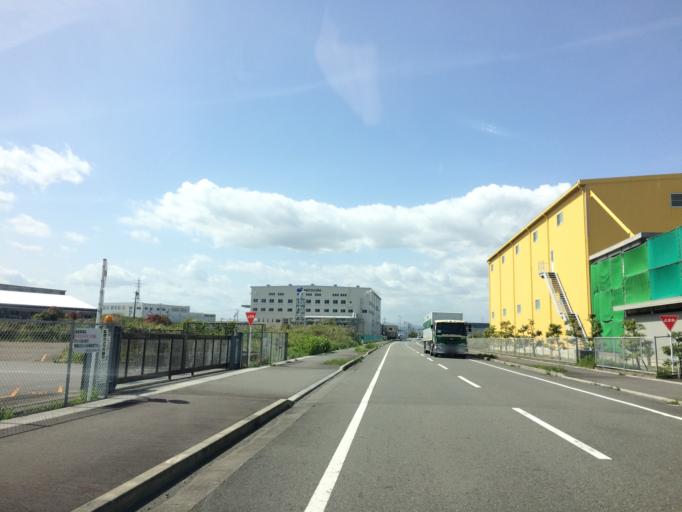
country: JP
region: Shizuoka
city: Fujieda
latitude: 34.7741
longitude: 138.2682
